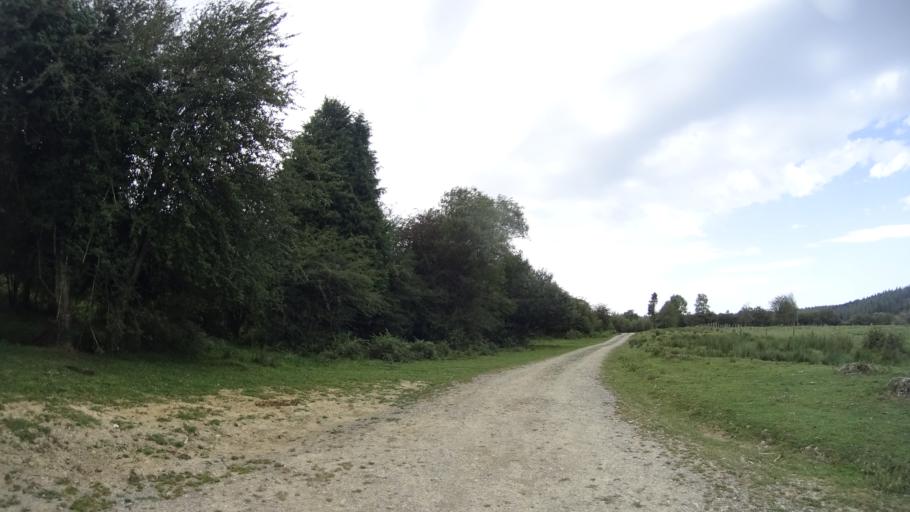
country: ES
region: Basque Country
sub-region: Bizkaia
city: Zeanuri
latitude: 43.0493
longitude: -2.7199
